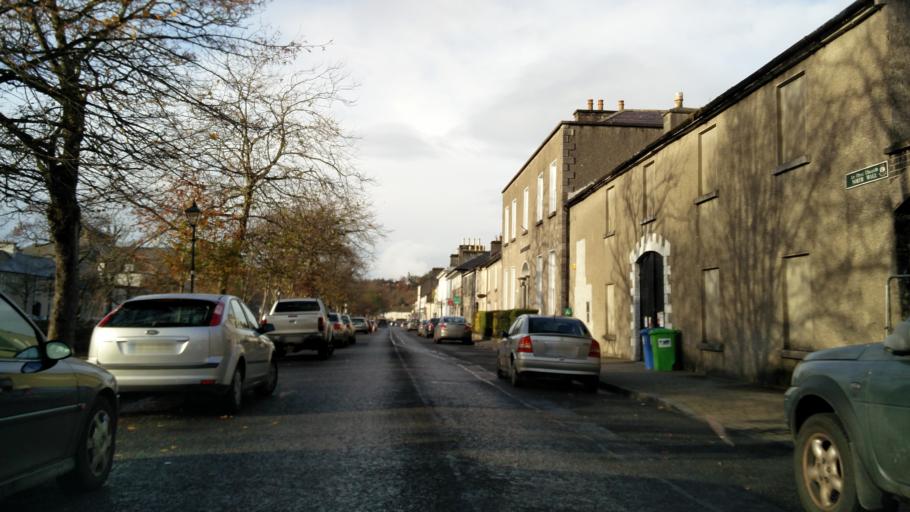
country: IE
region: Connaught
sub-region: Maigh Eo
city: Westport
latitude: 53.7997
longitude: -9.5188
